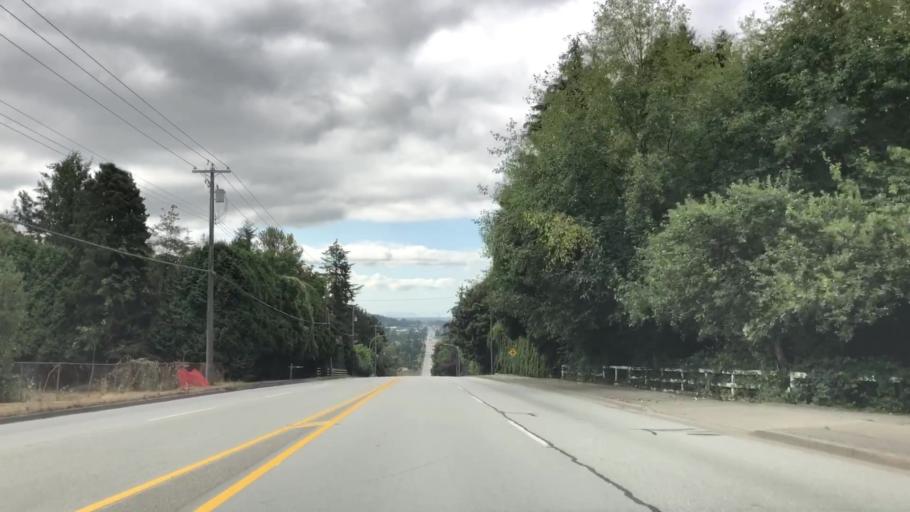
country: US
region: Washington
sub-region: Whatcom County
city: Blaine
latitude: 49.0364
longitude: -122.7353
